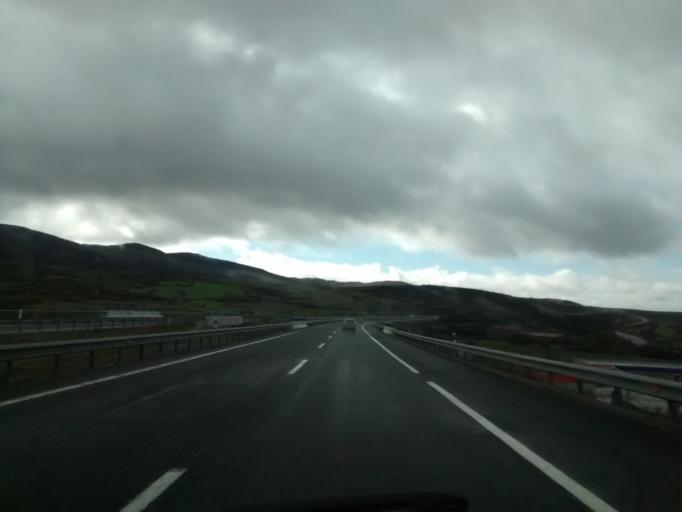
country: ES
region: Cantabria
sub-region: Provincia de Cantabria
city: Mataporquera
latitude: 42.8953
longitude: -4.1257
